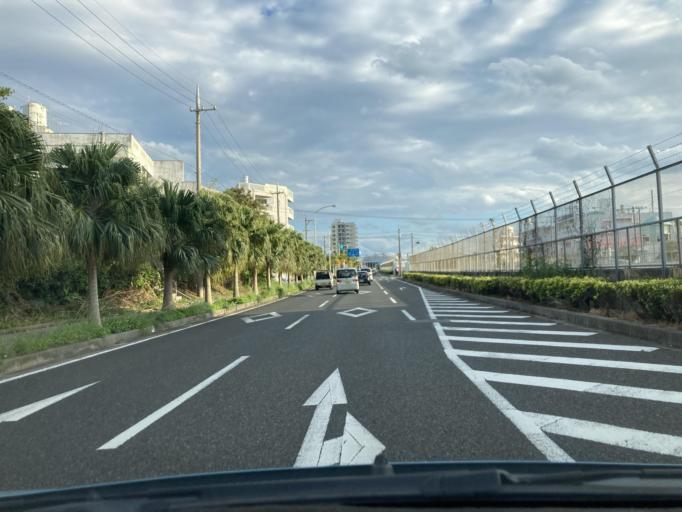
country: JP
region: Okinawa
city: Okinawa
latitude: 26.3261
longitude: 127.7871
